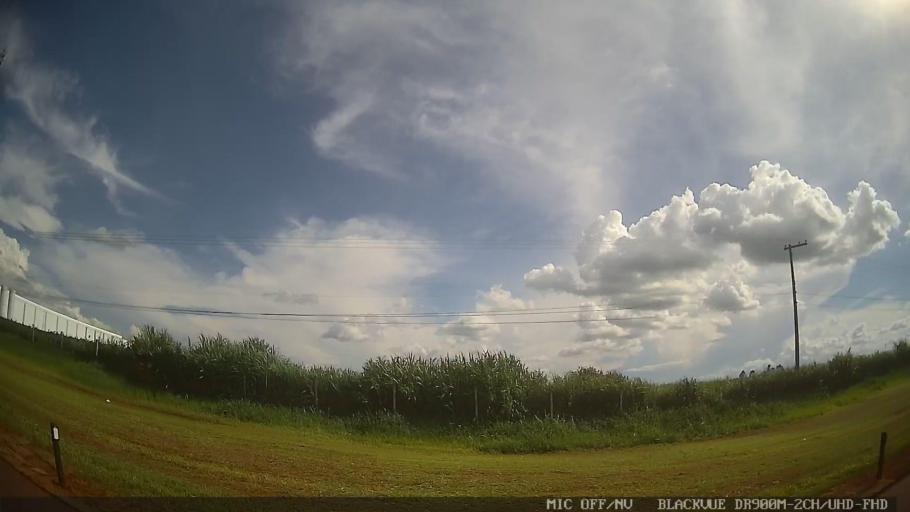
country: BR
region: Sao Paulo
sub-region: Laranjal Paulista
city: Laranjal Paulista
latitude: -23.0363
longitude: -47.8815
